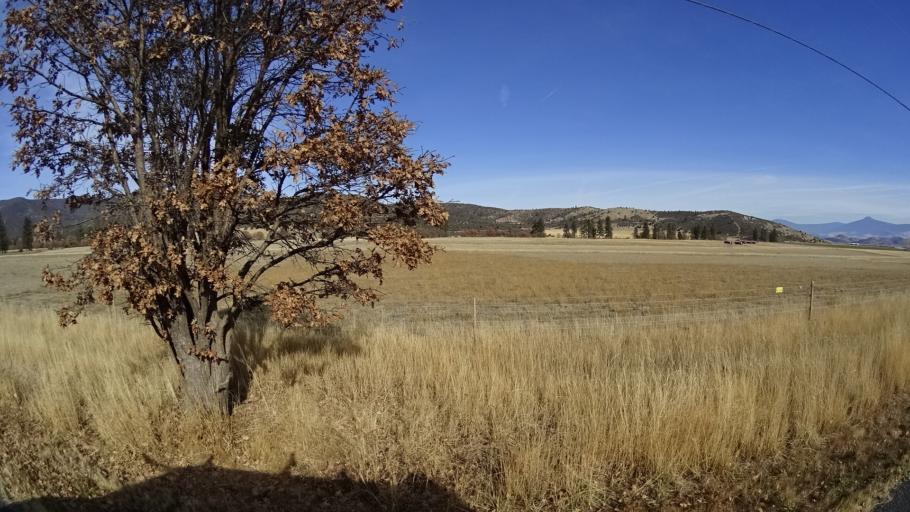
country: US
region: California
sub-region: Siskiyou County
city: Montague
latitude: 41.5388
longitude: -122.5803
